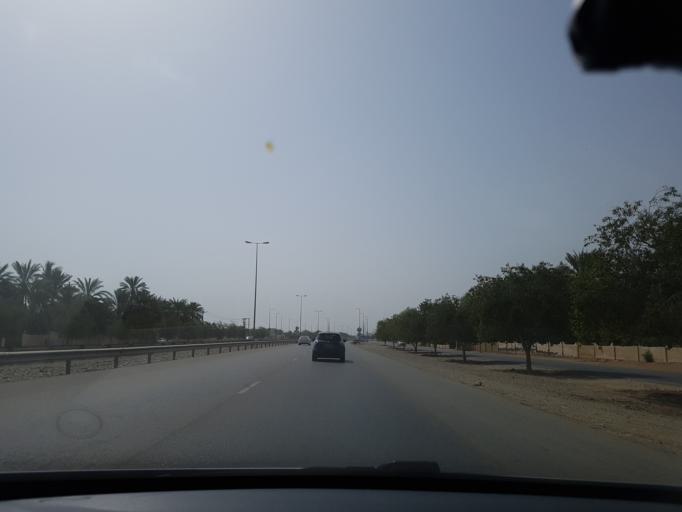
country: OM
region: Al Batinah
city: Al Khaburah
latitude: 23.9844
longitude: 57.0785
